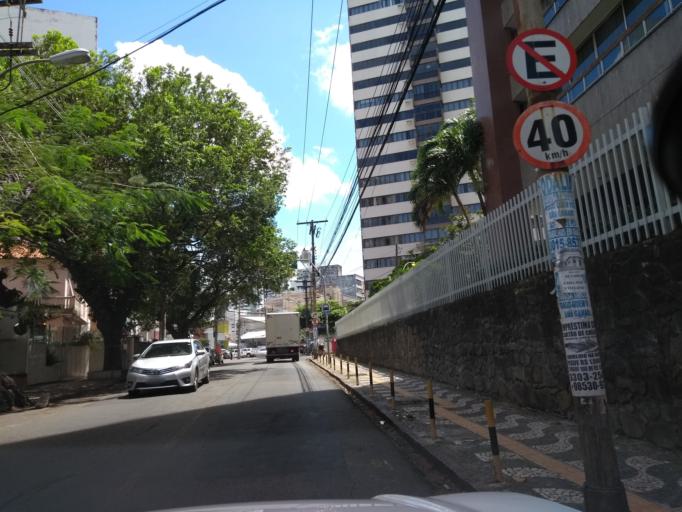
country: BR
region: Bahia
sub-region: Salvador
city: Salvador
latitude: -12.9972
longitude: -38.5188
